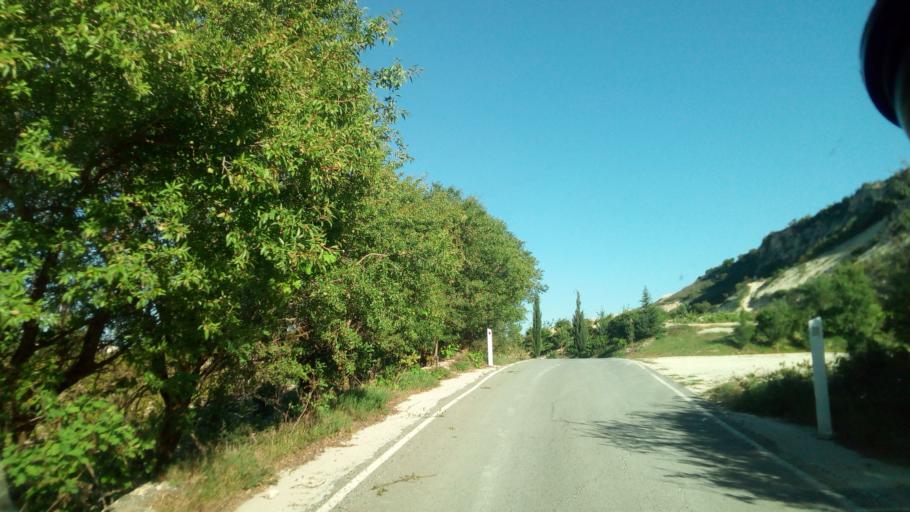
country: CY
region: Limassol
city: Pachna
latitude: 34.8649
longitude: 32.7832
